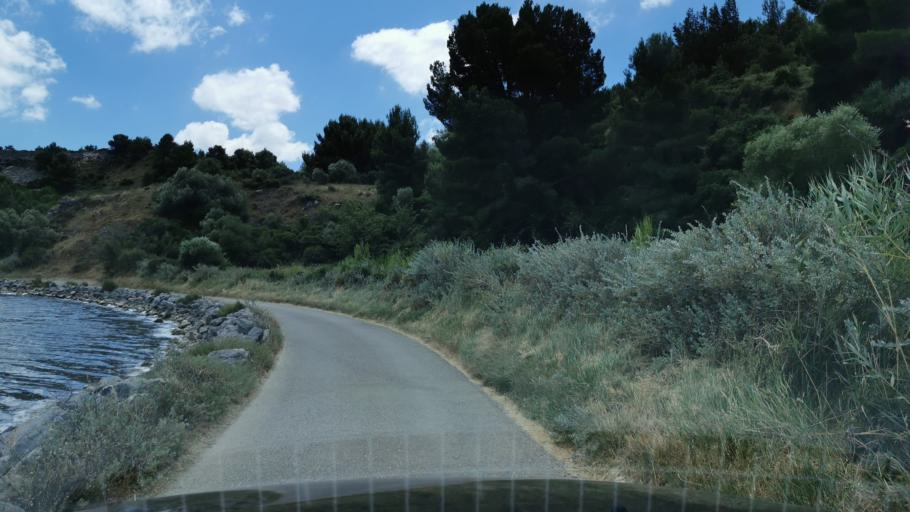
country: FR
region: Languedoc-Roussillon
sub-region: Departement de l'Aude
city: Peyriac-de-Mer
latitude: 43.0870
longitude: 2.9733
